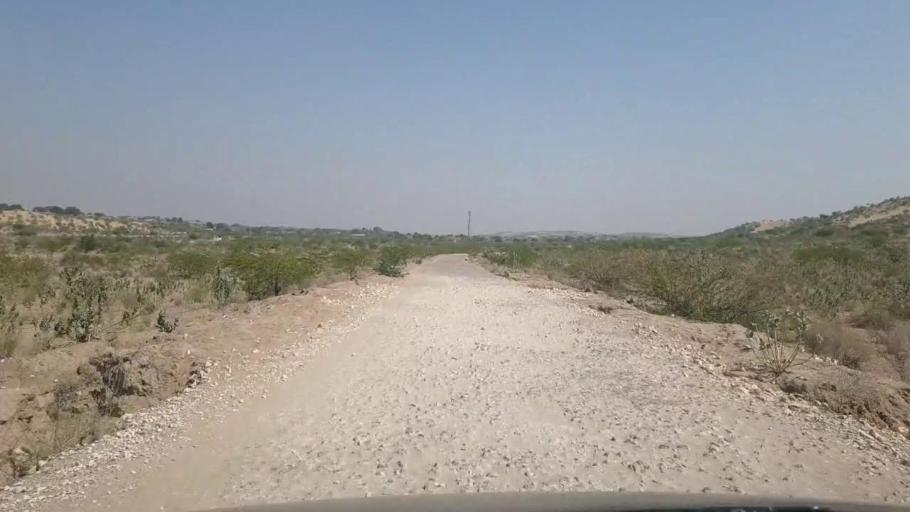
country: PK
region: Sindh
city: Chor
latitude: 25.6913
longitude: 70.1883
